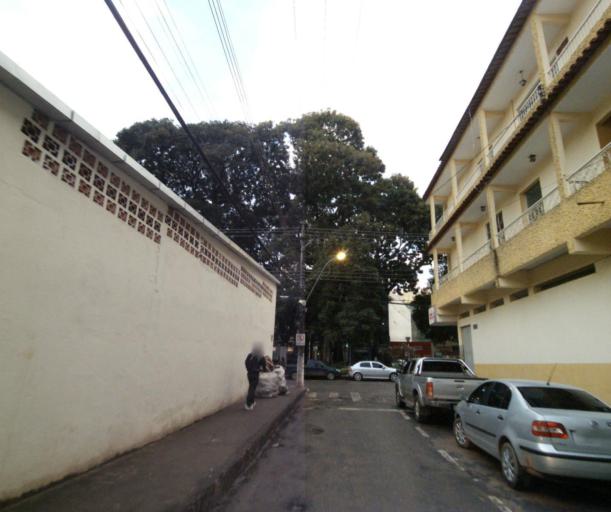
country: BR
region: Espirito Santo
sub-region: Muniz Freire
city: Muniz Freire
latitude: -20.4639
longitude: -41.4140
